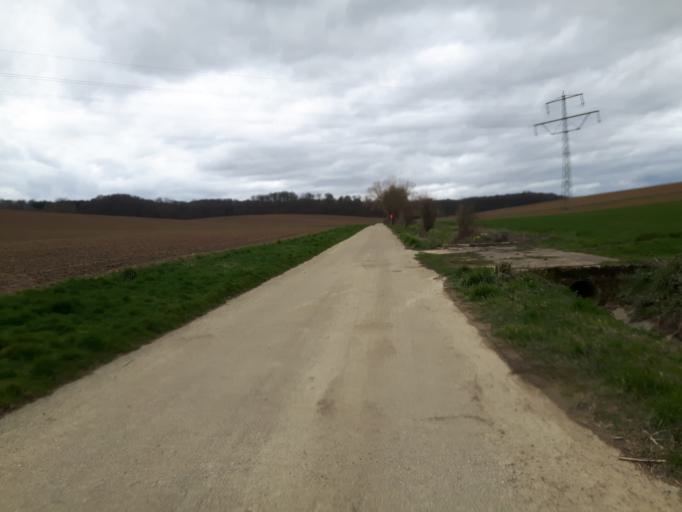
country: DE
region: Baden-Wuerttemberg
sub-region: Regierungsbezirk Stuttgart
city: Leingarten
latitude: 49.1777
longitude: 9.1072
